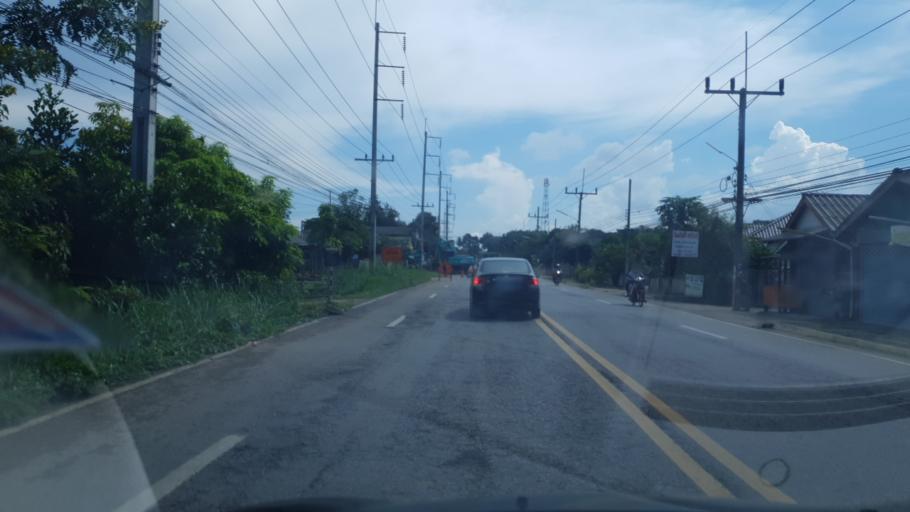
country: TH
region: Chiang Rai
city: Wiang Pa Pao
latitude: 19.3759
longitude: 99.5024
